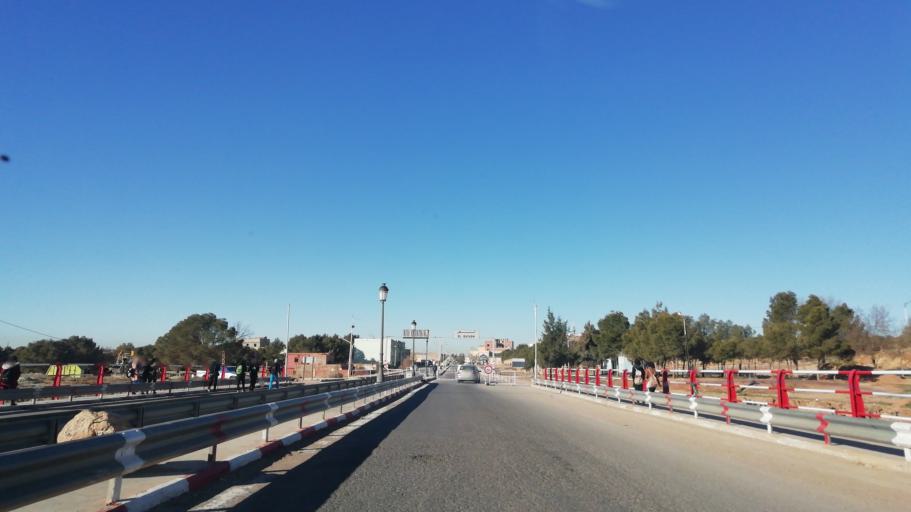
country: DZ
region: El Bayadh
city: El Bayadh
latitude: 33.6857
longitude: 1.0344
